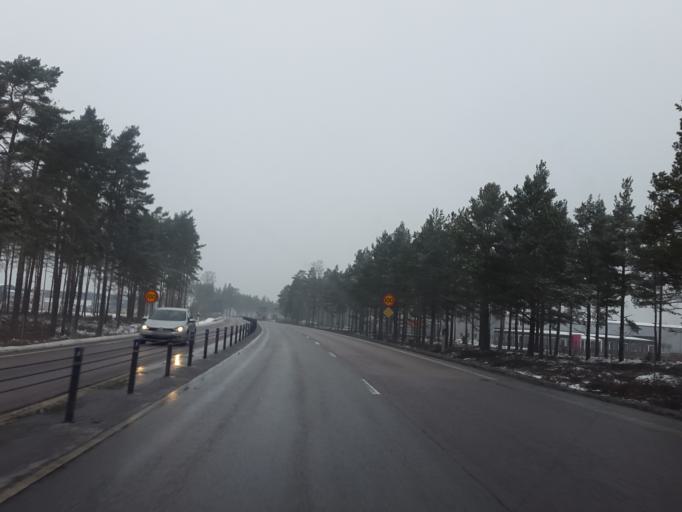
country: SE
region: Joenkoeping
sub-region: Jonkopings Kommun
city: Jonkoping
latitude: 57.7659
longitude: 14.0966
